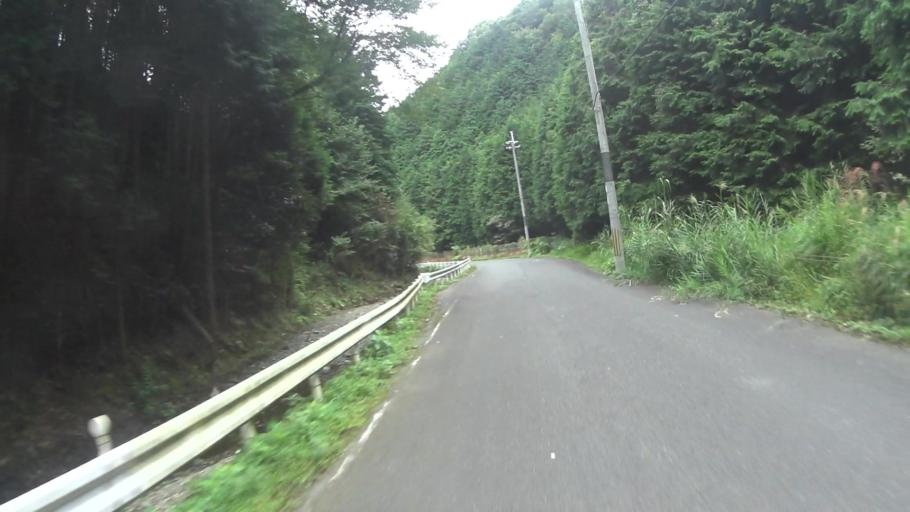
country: JP
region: Kyoto
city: Tanabe
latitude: 34.8133
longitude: 135.8633
